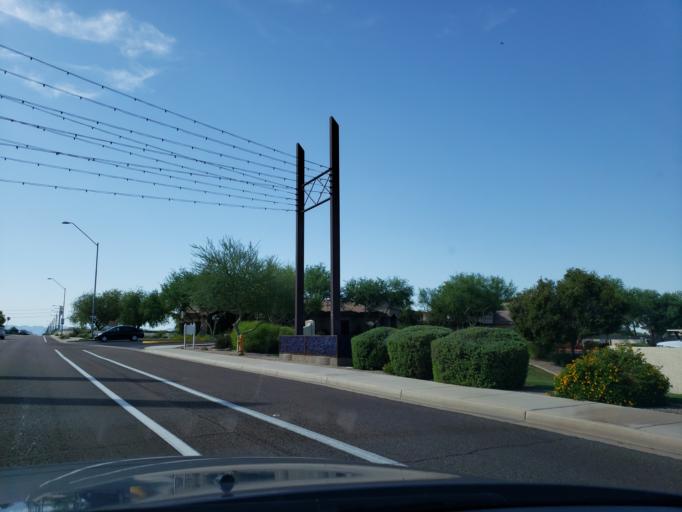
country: US
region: Arizona
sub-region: Maricopa County
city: Sun City
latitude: 33.6249
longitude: -112.2375
